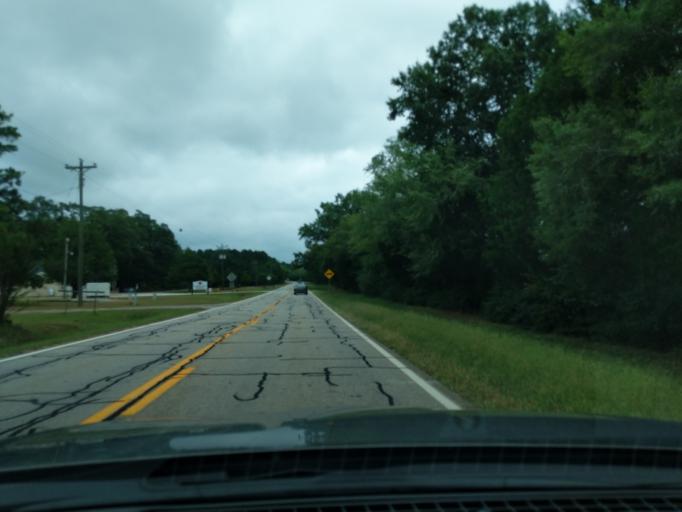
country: US
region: Georgia
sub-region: Columbia County
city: Appling
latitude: 33.6061
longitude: -82.3945
